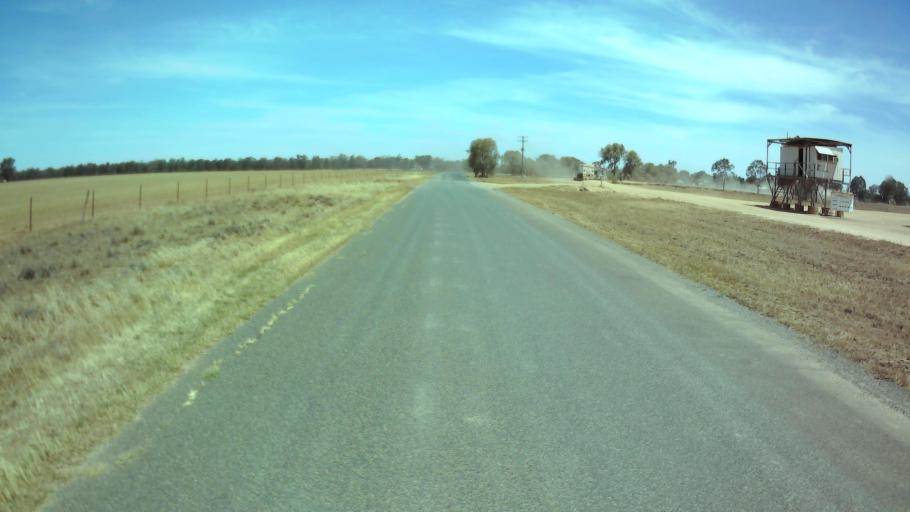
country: AU
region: New South Wales
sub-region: Weddin
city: Grenfell
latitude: -33.8338
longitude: 147.7460
